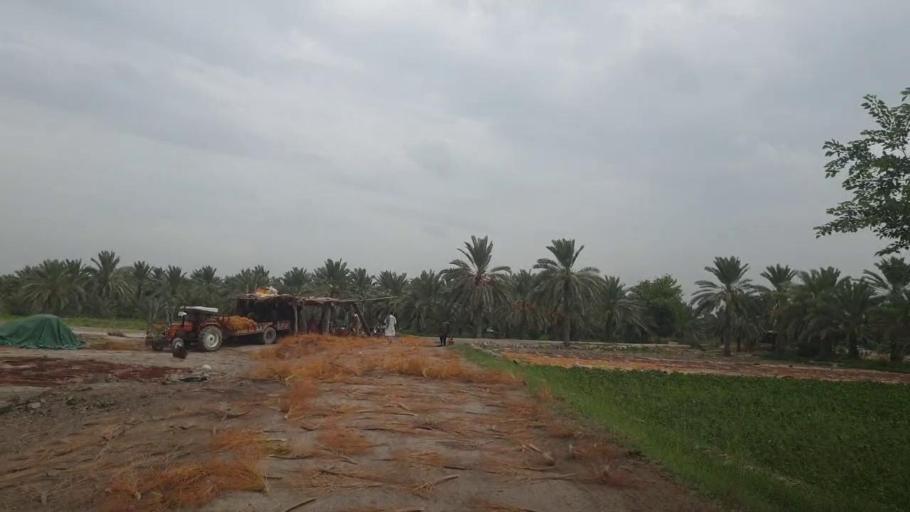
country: PK
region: Sindh
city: Khairpur
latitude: 27.5917
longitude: 68.7404
